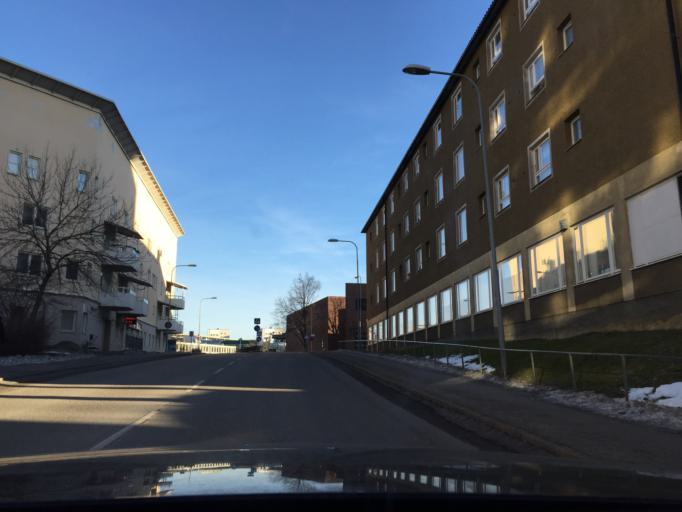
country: SE
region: Stockholm
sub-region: Jarfalla Kommun
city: Jakobsberg
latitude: 59.3635
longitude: 17.8686
